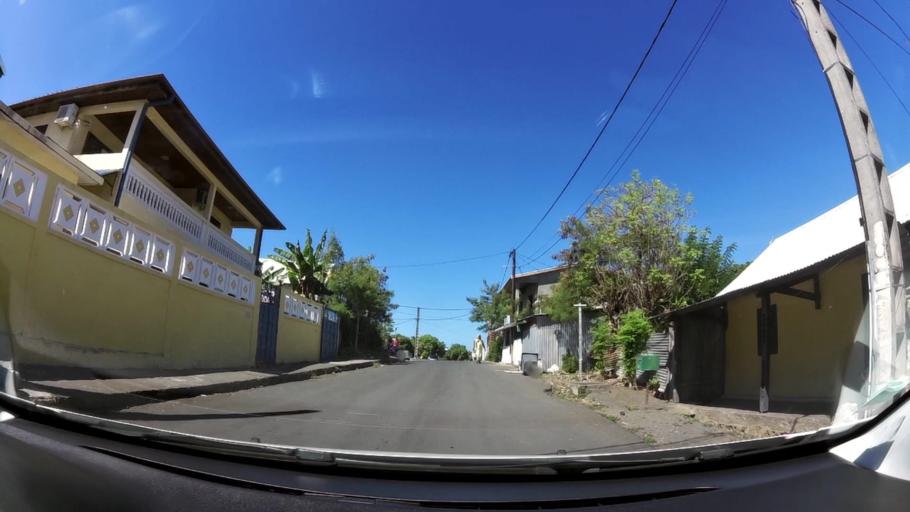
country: YT
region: Pamandzi
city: Pamandzi
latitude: -12.7974
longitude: 45.2826
